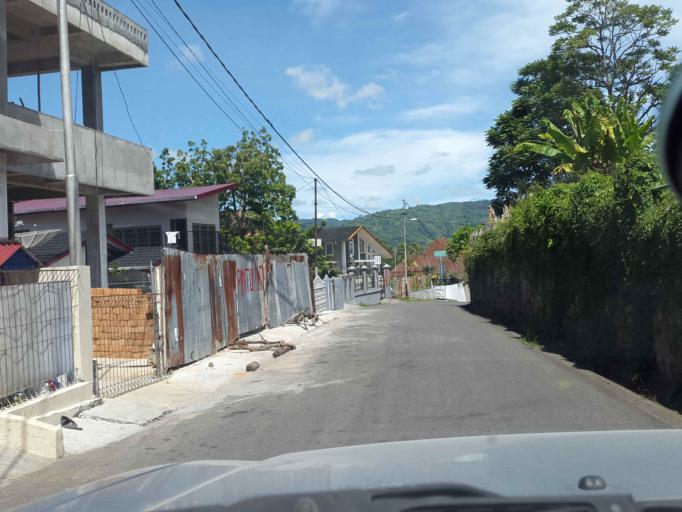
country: ID
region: West Sumatra
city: Bukittinggi
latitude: -0.3064
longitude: 100.3676
